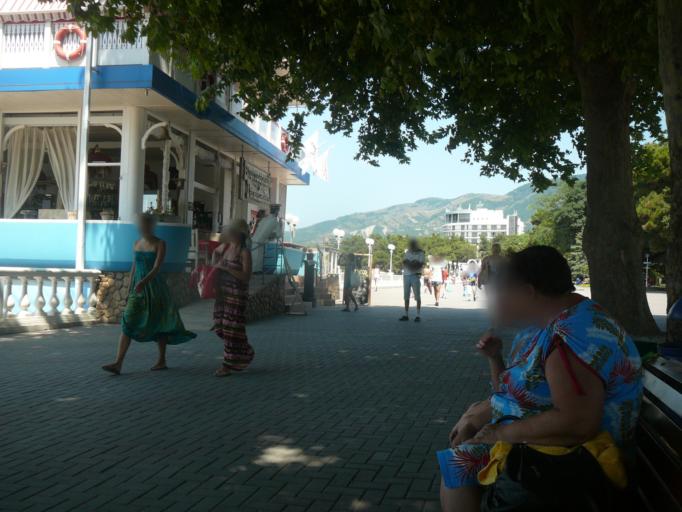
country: RU
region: Krasnodarskiy
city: Gelendzhik
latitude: 44.5628
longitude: 38.0769
